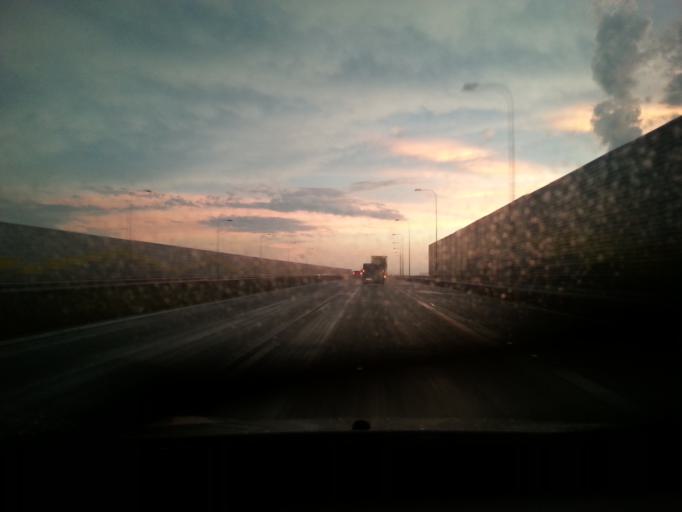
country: PL
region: Lodz Voivodeship
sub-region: Powiat laski
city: Lask
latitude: 51.5536
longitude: 19.0829
